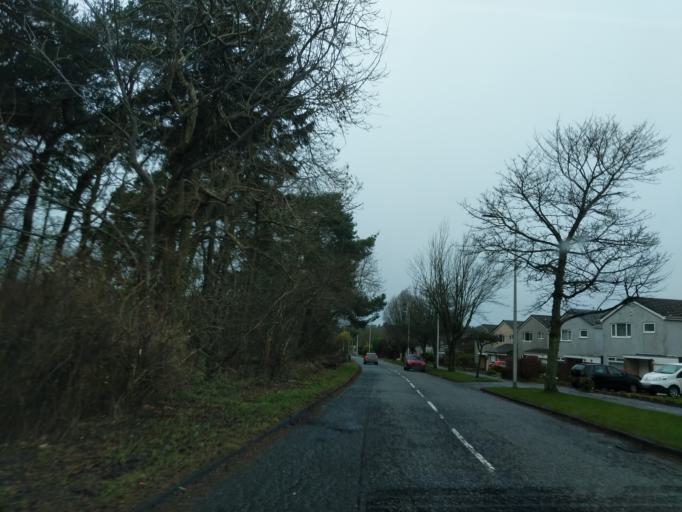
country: GB
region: Scotland
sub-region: Edinburgh
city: Balerno
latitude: 55.8771
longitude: -3.3480
